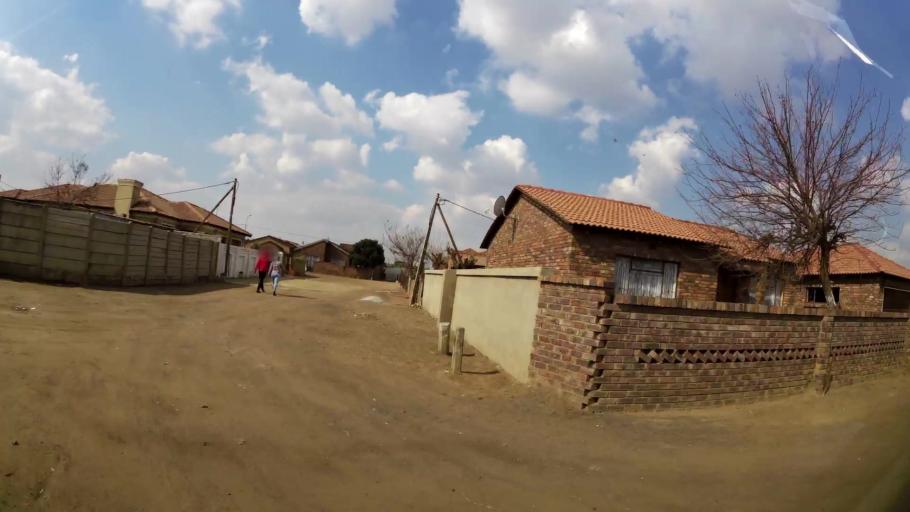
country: ZA
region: Gauteng
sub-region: Ekurhuleni Metropolitan Municipality
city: Springs
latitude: -26.1260
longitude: 28.4758
